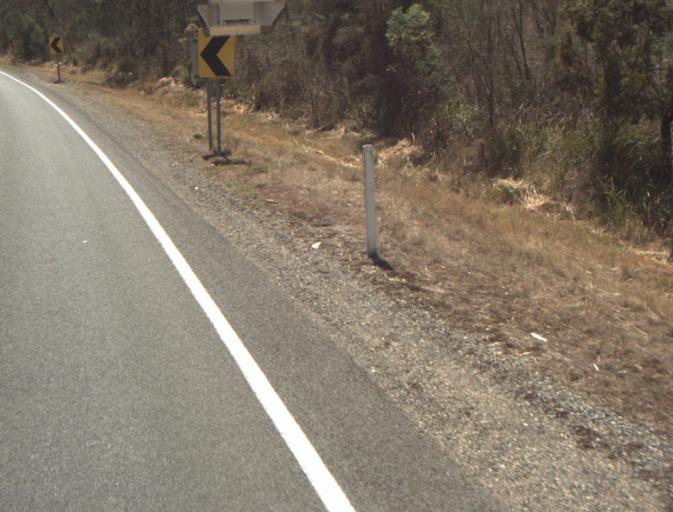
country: AU
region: Tasmania
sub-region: Launceston
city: Mayfield
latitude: -41.3635
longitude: 147.1450
